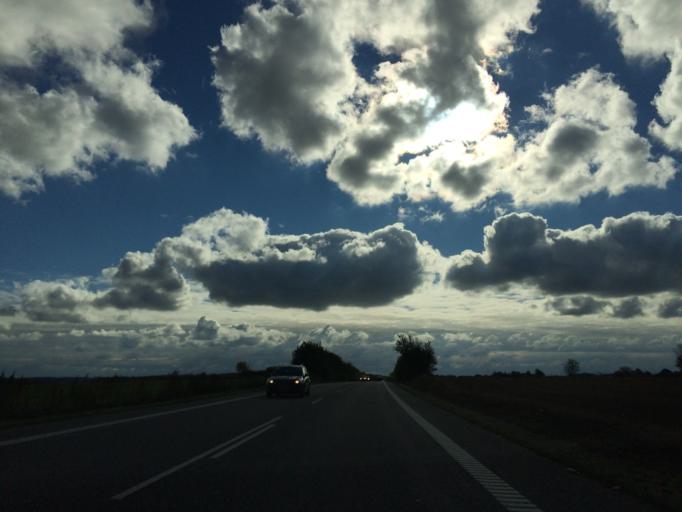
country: DK
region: Central Jutland
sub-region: Skanderborg Kommune
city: Ry
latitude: 56.1345
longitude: 9.7961
